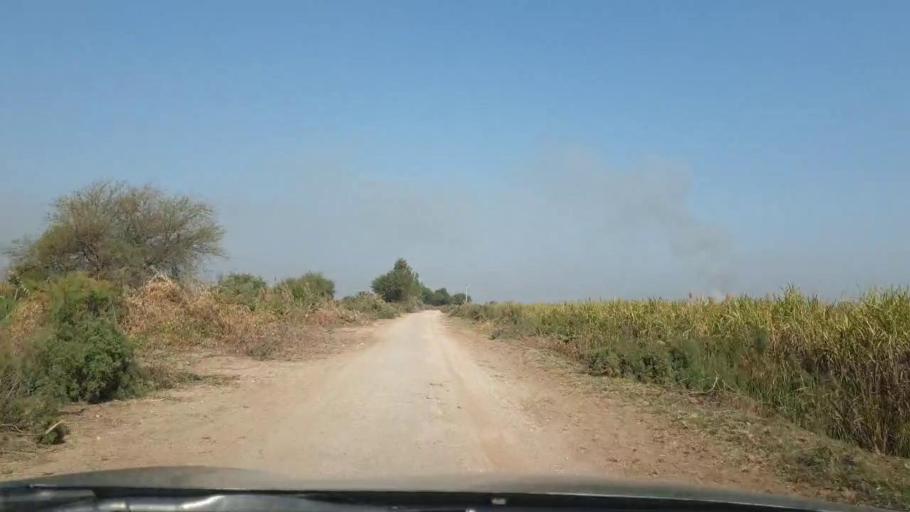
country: PK
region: Sindh
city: Berani
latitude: 25.6431
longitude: 68.8963
